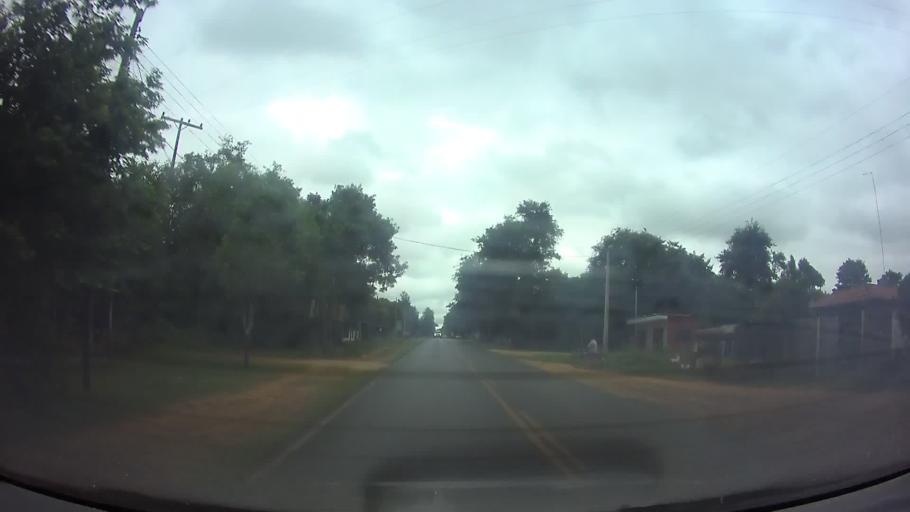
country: PY
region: Central
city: Guarambare
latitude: -25.5454
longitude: -57.4992
